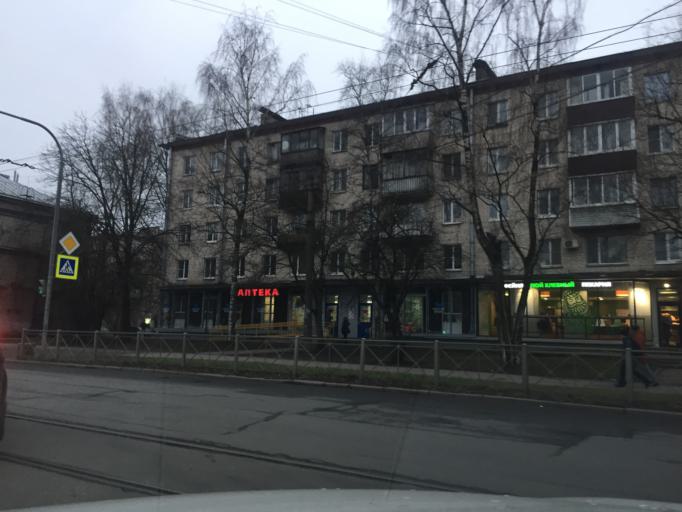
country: RU
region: St.-Petersburg
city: Sosnovka
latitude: 60.0164
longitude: 30.3677
